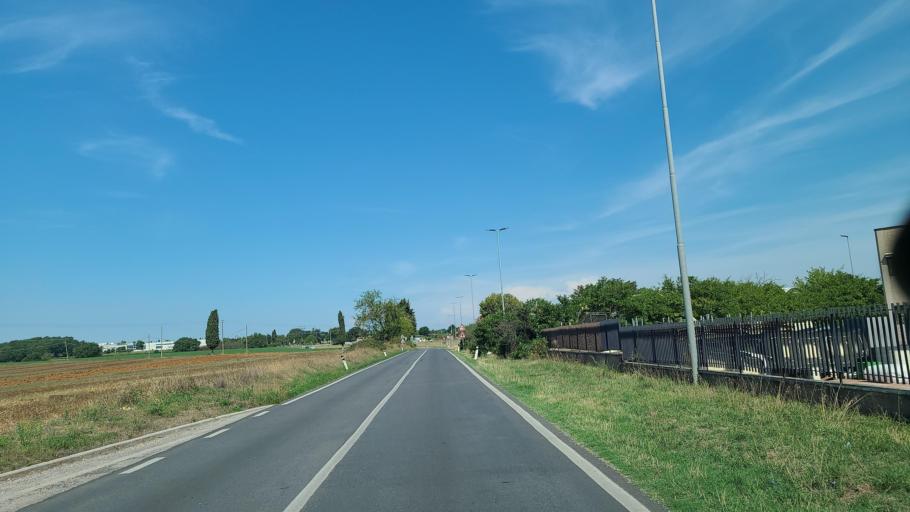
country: IT
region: Tuscany
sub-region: Provincia di Siena
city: Staggia
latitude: 43.3998
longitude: 11.1760
